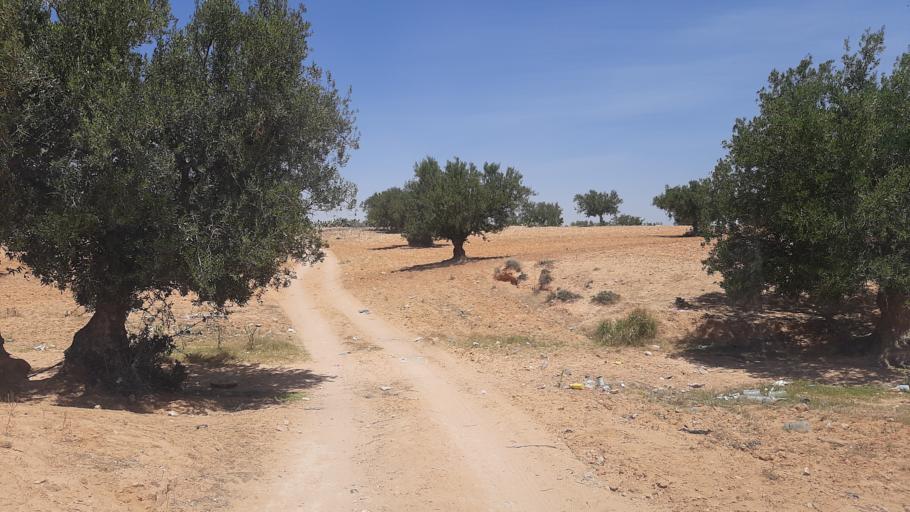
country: TN
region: Safaqis
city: Bi'r `Ali Bin Khalifah
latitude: 34.5663
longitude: 10.3460
